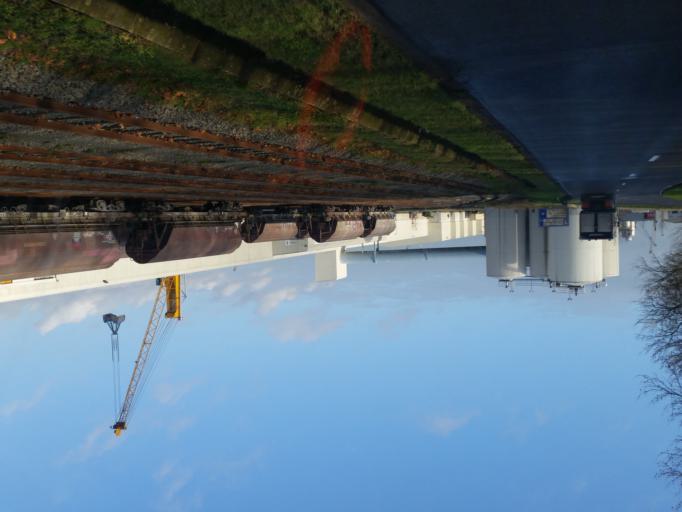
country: BE
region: Flanders
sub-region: Provincie Antwerpen
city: Antwerpen
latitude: 51.2433
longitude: 4.3920
